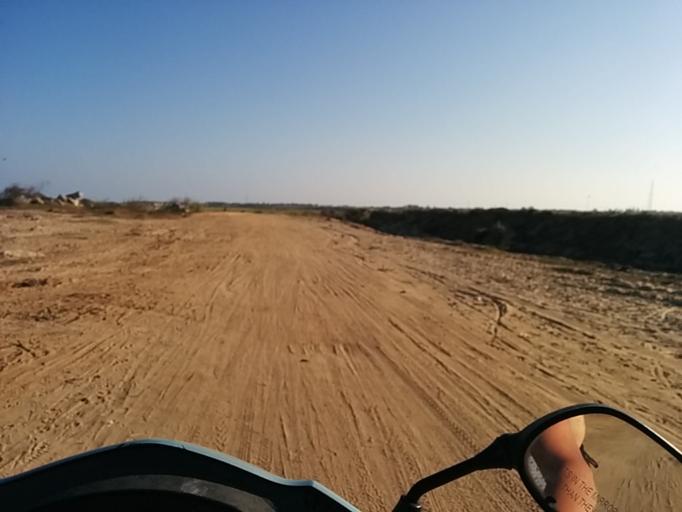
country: IN
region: Pondicherry
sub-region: Puducherry
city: Puducherry
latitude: 11.9127
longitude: 79.8297
